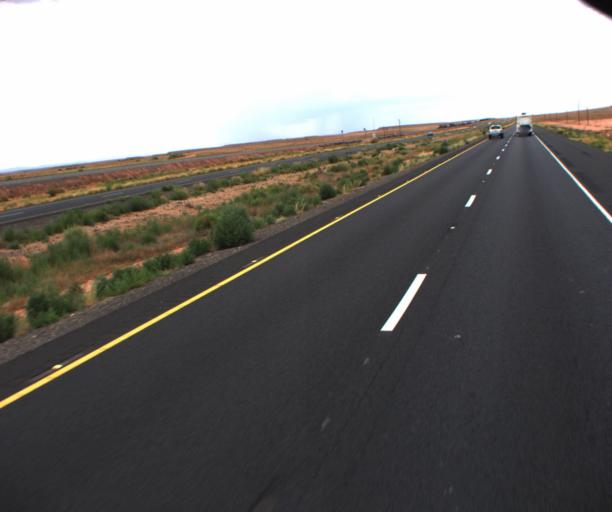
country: US
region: Arizona
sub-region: Coconino County
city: LeChee
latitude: 35.0506
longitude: -110.7773
